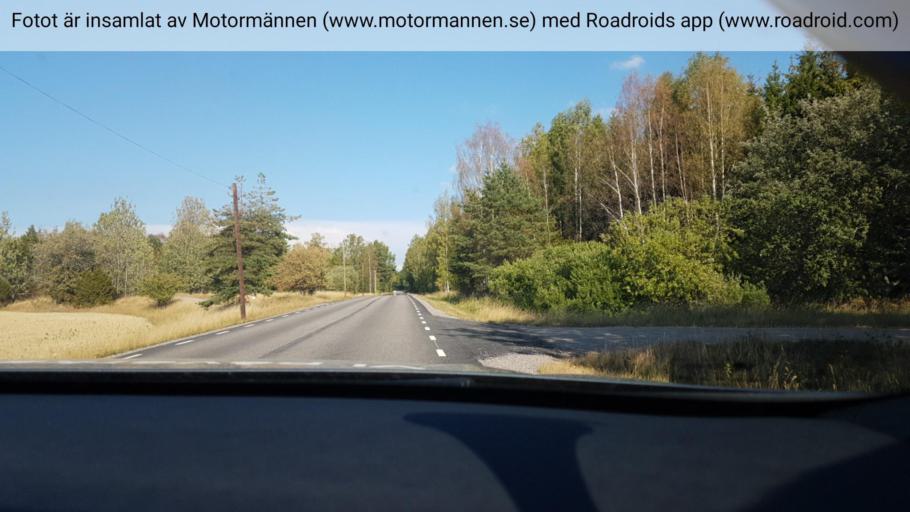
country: SE
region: Vaestra Goetaland
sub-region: Gotene Kommun
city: Goetene
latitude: 58.6305
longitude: 13.5095
